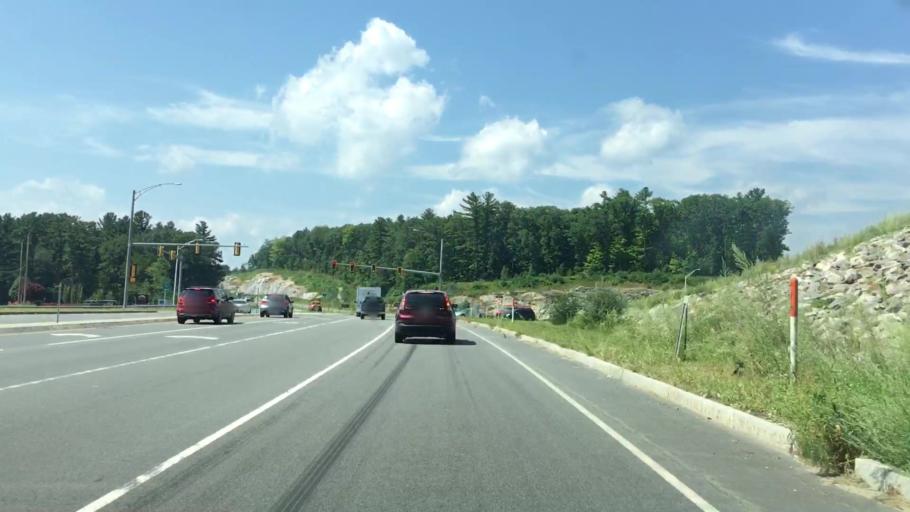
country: US
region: New Hampshire
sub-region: Rockingham County
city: Windham
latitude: 42.8094
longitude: -71.2730
